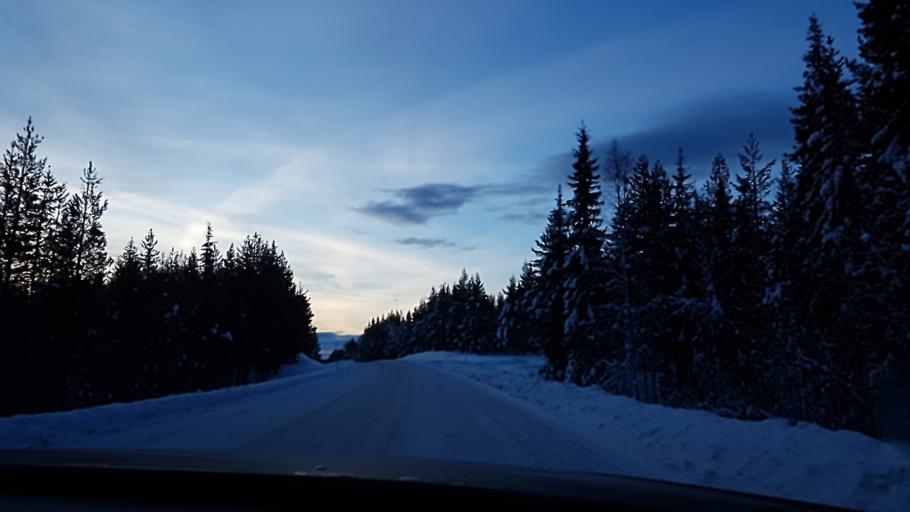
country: SE
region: Norrbotten
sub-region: Arvidsjaurs Kommun
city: Arvidsjaur
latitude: 65.9362
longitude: 19.4637
